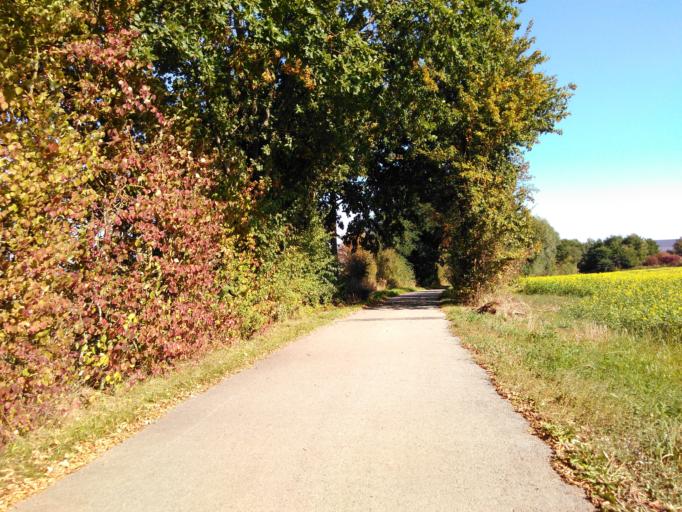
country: LU
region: Diekirch
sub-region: Canton de Redange
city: Beckerich
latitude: 49.7273
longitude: 5.9000
